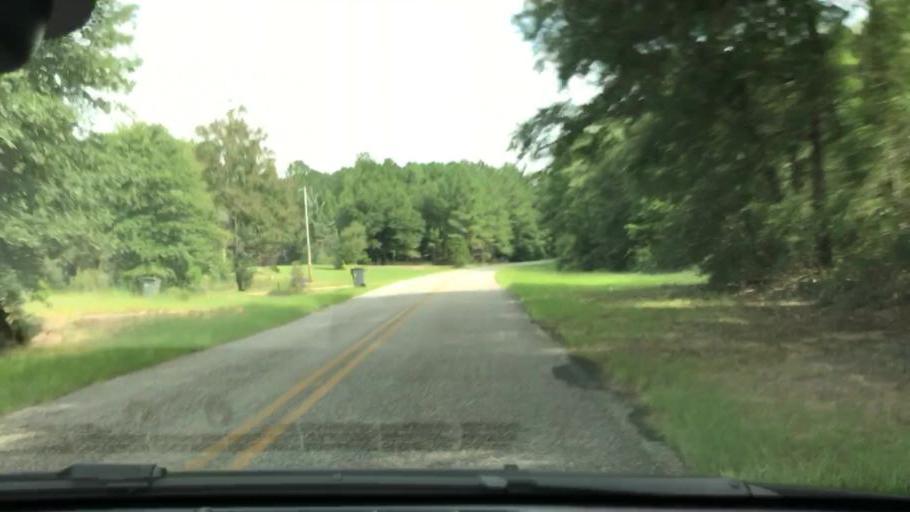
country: US
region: Georgia
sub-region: Early County
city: Blakely
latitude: 31.5044
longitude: -84.9452
